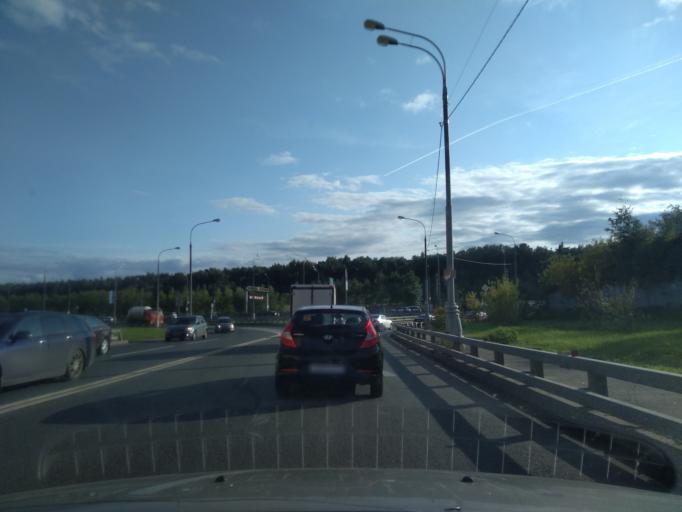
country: RU
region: Moscow
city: Rublevo
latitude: 55.7888
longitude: 37.3834
